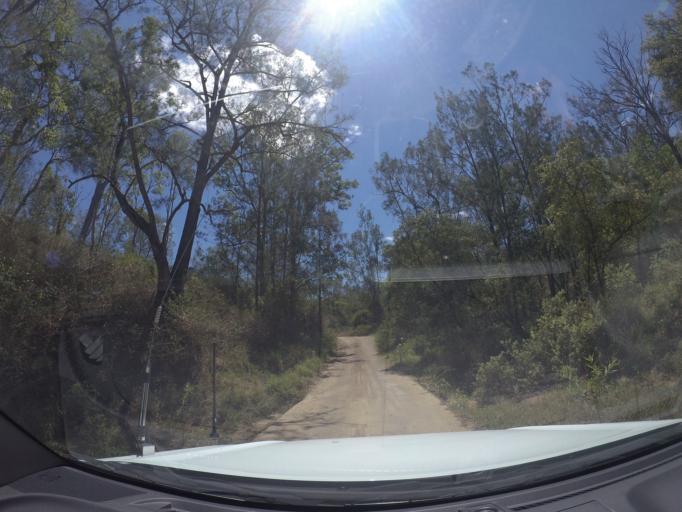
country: AU
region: Queensland
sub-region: Ipswich
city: Springfield Lakes
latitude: -27.8117
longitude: 152.8506
